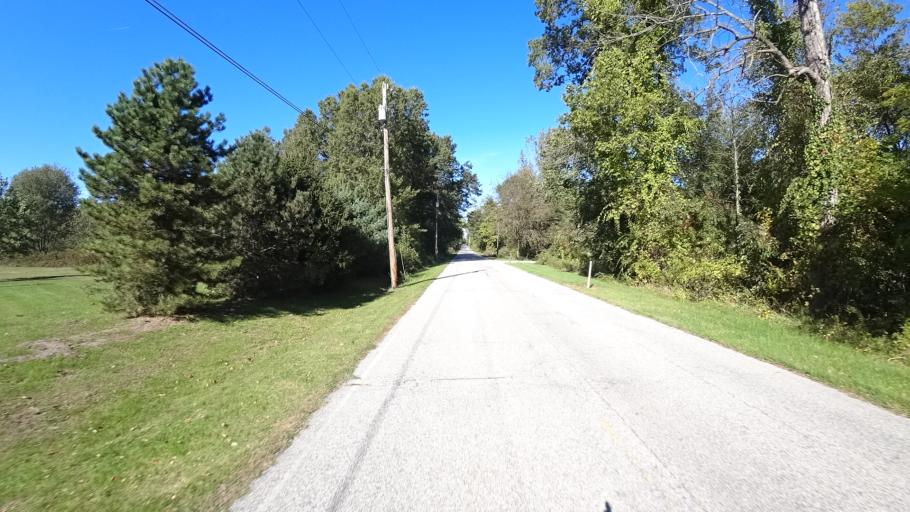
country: US
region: Indiana
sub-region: LaPorte County
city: Long Beach
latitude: 41.7426
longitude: -86.8161
